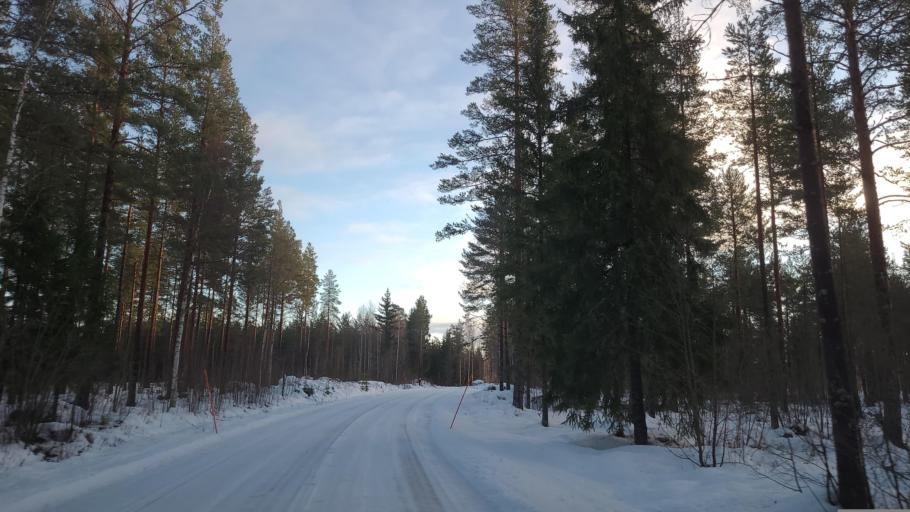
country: SE
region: Gaevleborg
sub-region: Bollnas Kommun
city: Kilafors
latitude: 61.4012
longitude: 16.6466
